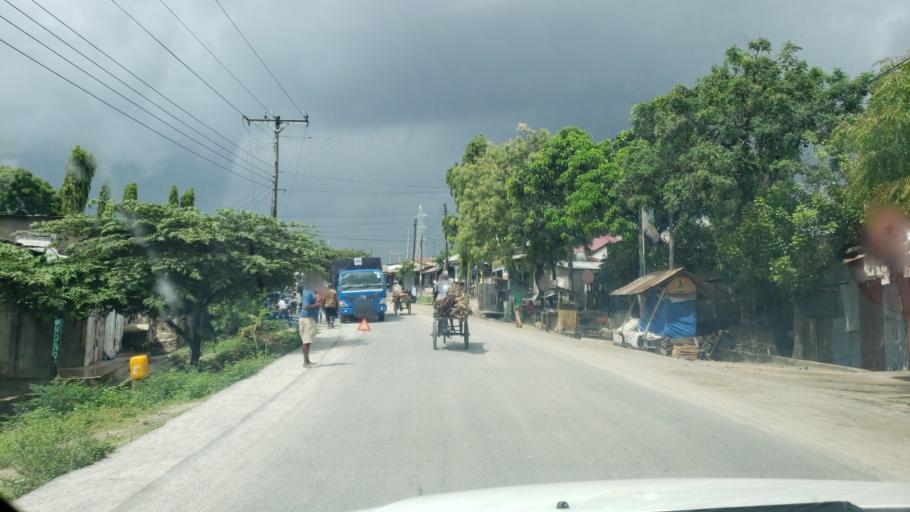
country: TZ
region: Dar es Salaam
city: Magomeni
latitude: -6.8076
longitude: 39.2413
